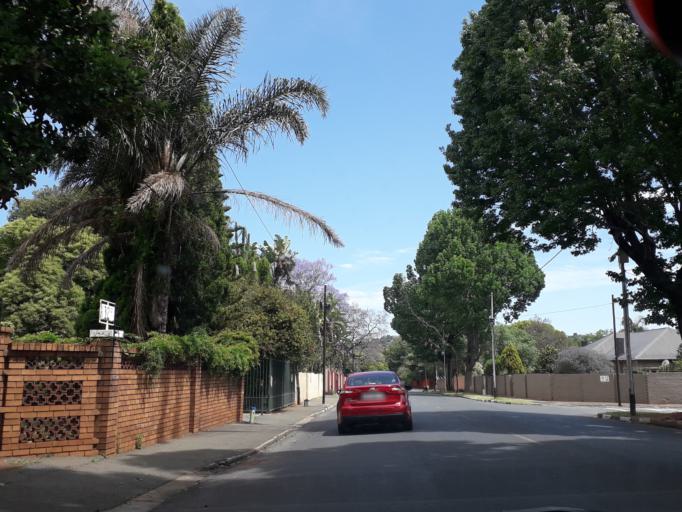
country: ZA
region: Gauteng
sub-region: City of Johannesburg Metropolitan Municipality
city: Johannesburg
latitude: -26.1493
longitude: 28.0903
